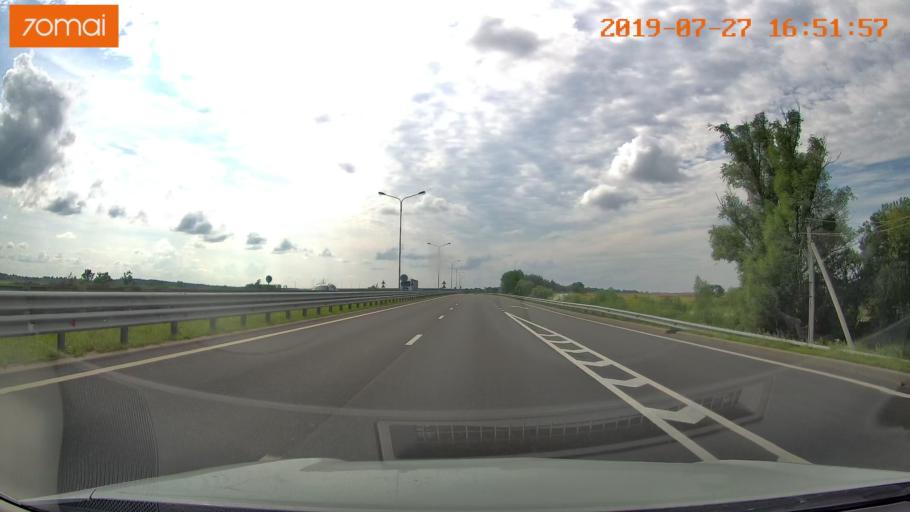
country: RU
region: Kaliningrad
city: Gvardeysk
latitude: 54.6838
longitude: 20.8731
